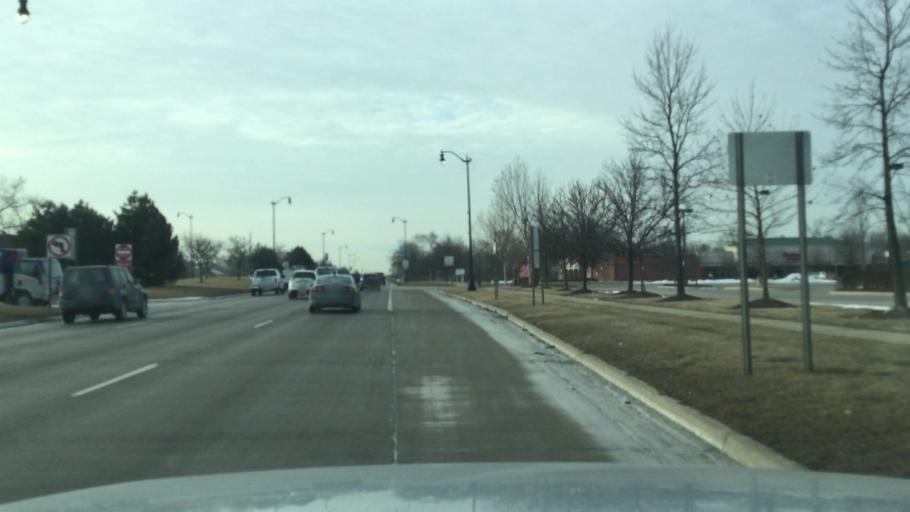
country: US
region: Michigan
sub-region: Wayne County
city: Taylor
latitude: 42.2251
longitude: -83.2695
